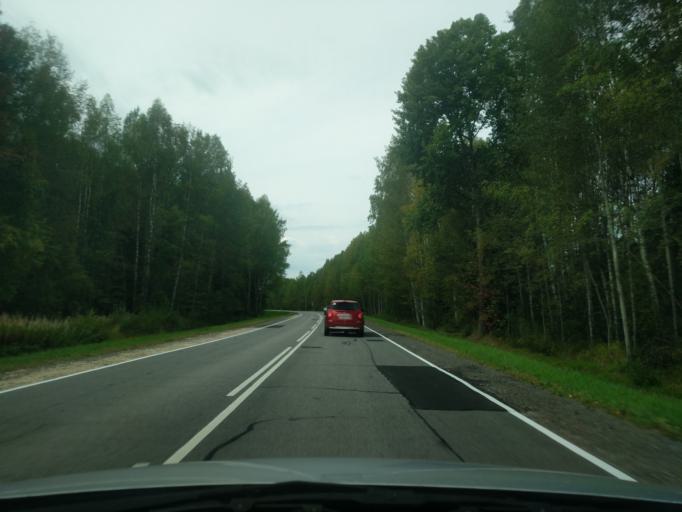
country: RU
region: Kirov
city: Kotel'nich
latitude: 58.2714
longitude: 48.0760
